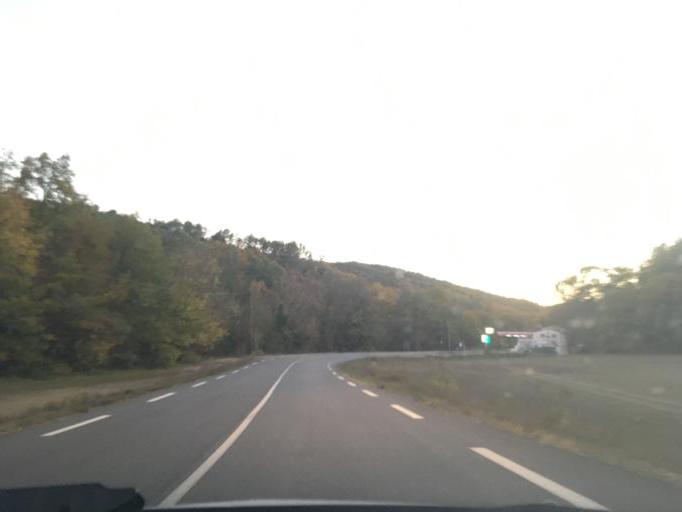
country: FR
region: Provence-Alpes-Cote d'Azur
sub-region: Departement du Var
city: Montferrat
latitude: 43.6073
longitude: 6.4809
